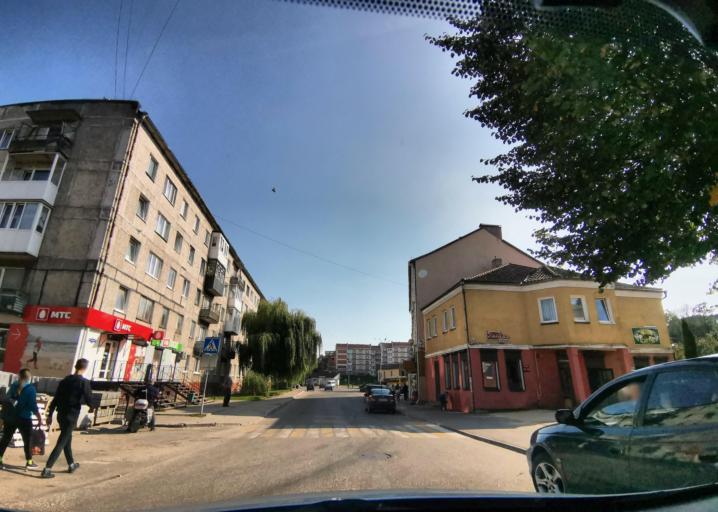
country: RU
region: Kaliningrad
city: Neman
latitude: 55.0378
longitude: 22.0300
